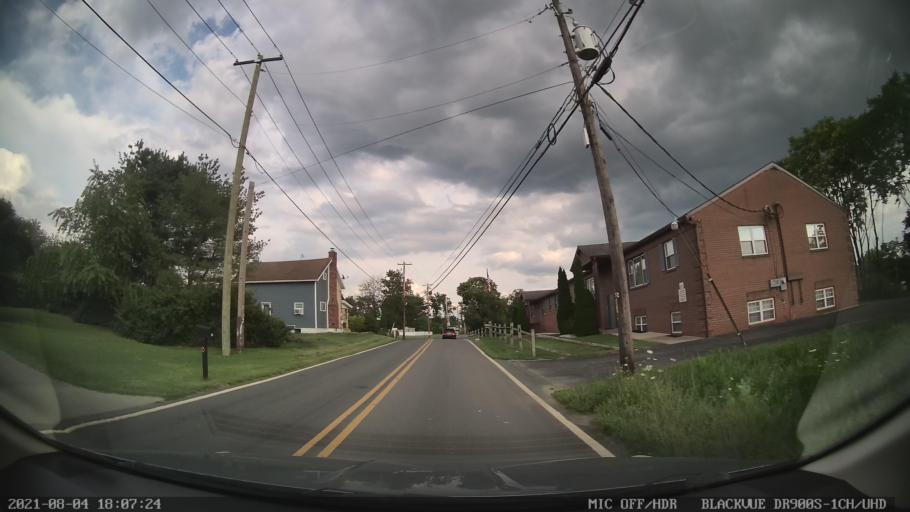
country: US
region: Pennsylvania
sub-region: Lehigh County
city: Ancient Oaks
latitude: 40.5610
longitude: -75.5773
